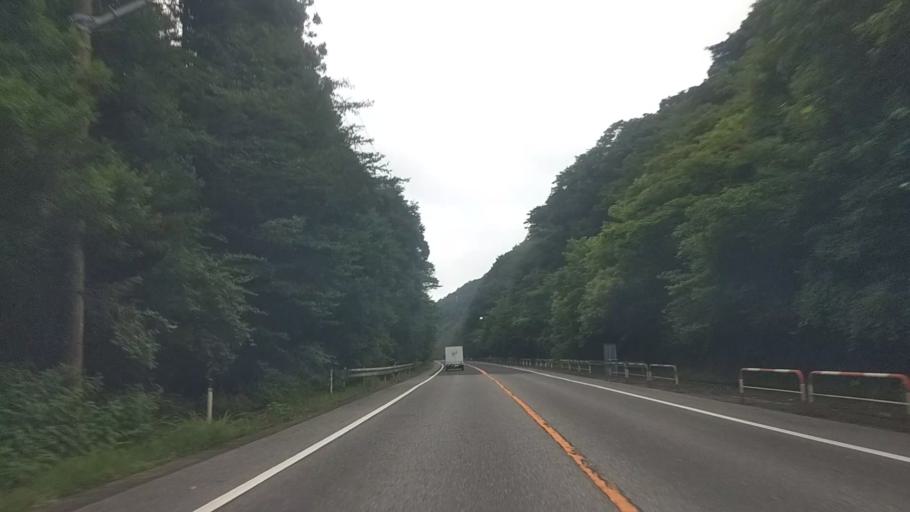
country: JP
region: Chiba
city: Kawaguchi
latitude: 35.1702
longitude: 140.0597
